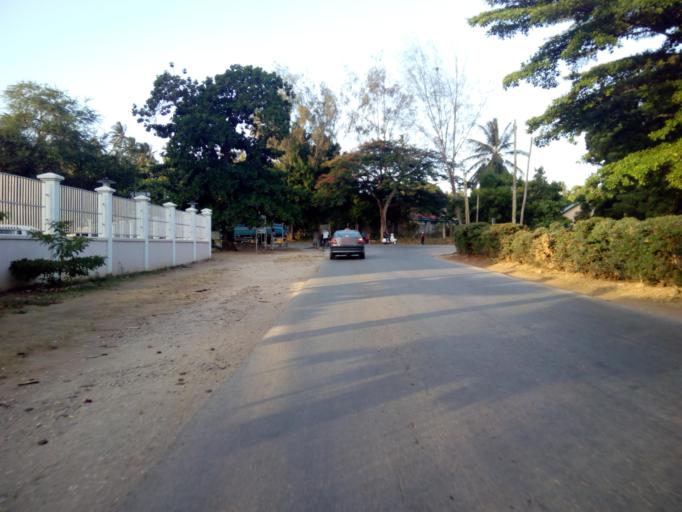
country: TZ
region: Zanzibar Urban/West
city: Zanzibar
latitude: -6.2003
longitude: 39.2109
